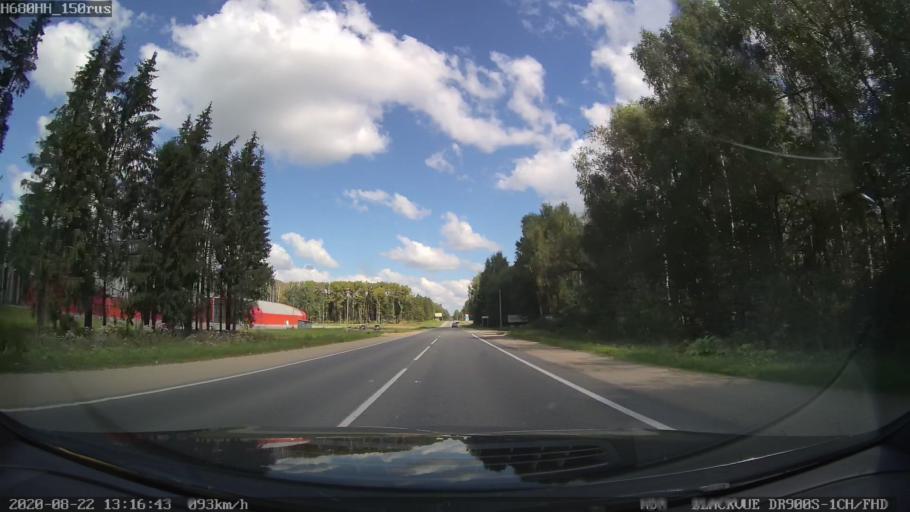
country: RU
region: Tverskaya
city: Bezhetsk
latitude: 57.7670
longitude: 36.6609
